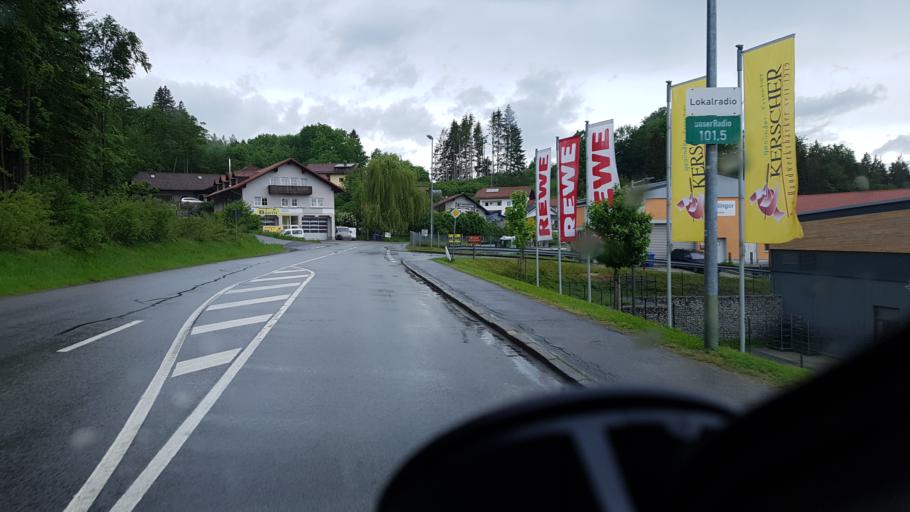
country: DE
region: Bavaria
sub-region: Lower Bavaria
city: Waldkirchen
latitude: 48.7222
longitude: 13.6138
